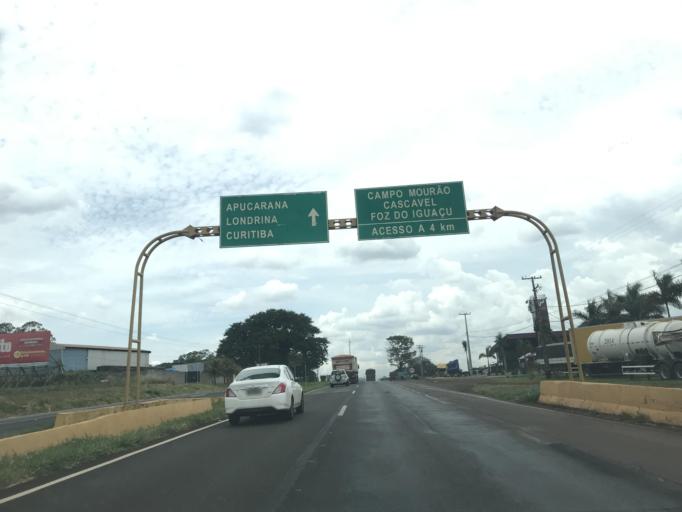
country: BR
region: Parana
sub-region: Maringa
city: Maringa
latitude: -23.3986
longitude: -52.0028
